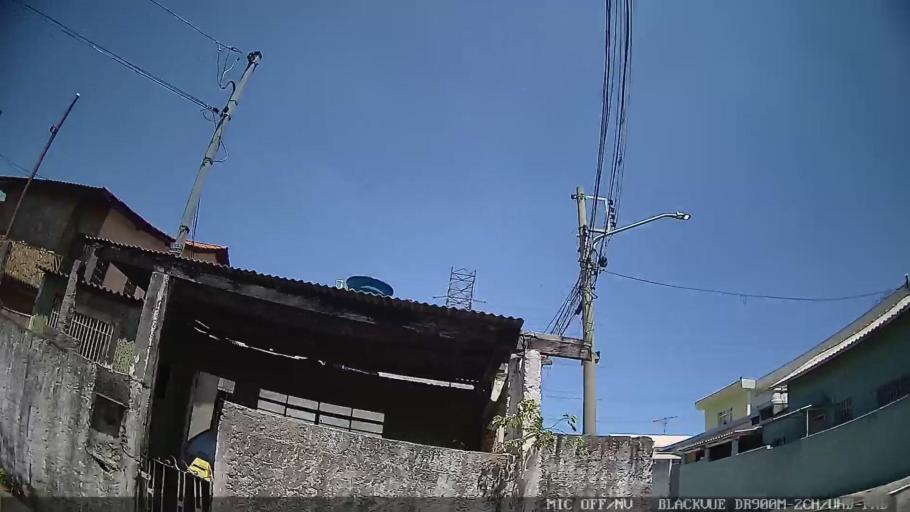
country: BR
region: Sao Paulo
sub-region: Sao Caetano Do Sul
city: Sao Caetano do Sul
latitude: -23.5957
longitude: -46.5409
